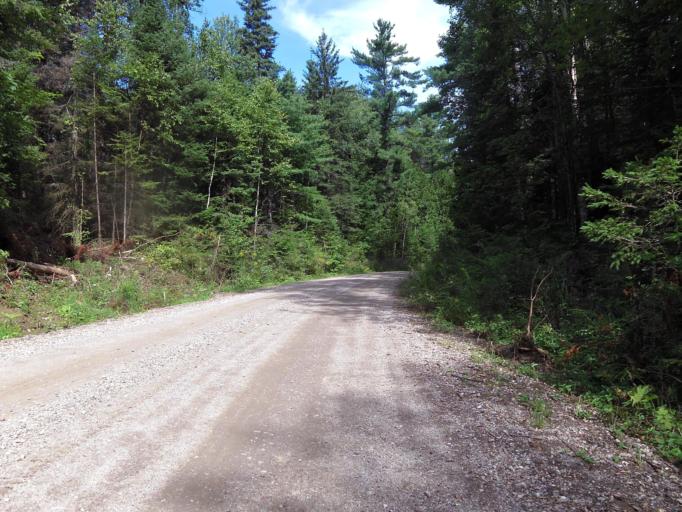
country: CA
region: Ontario
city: Renfrew
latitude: 45.1153
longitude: -76.7263
